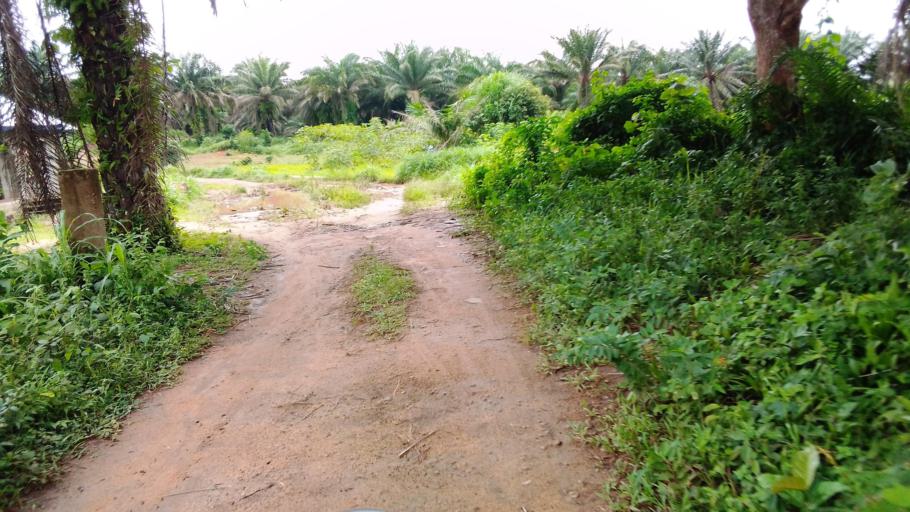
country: SL
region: Eastern Province
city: Kenema
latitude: 7.8687
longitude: -11.1682
